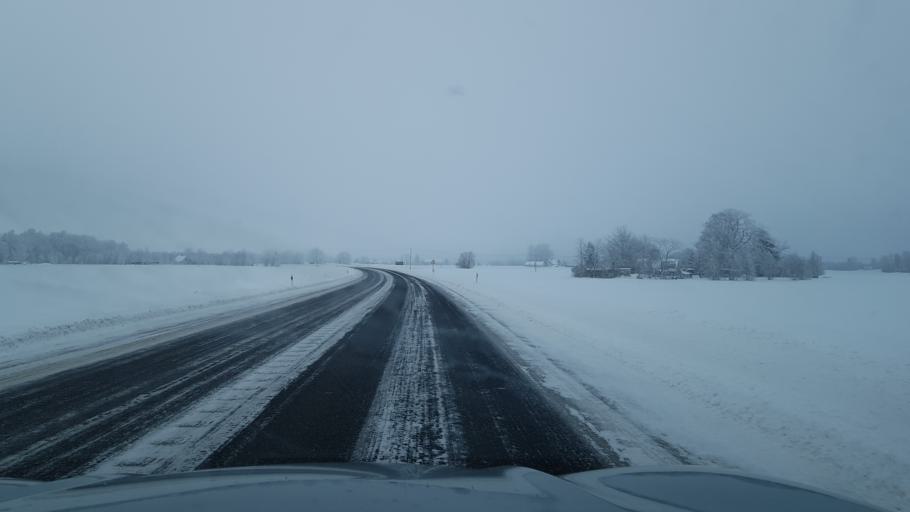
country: EE
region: Ida-Virumaa
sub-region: Johvi vald
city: Johvi
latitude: 59.2506
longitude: 27.3764
